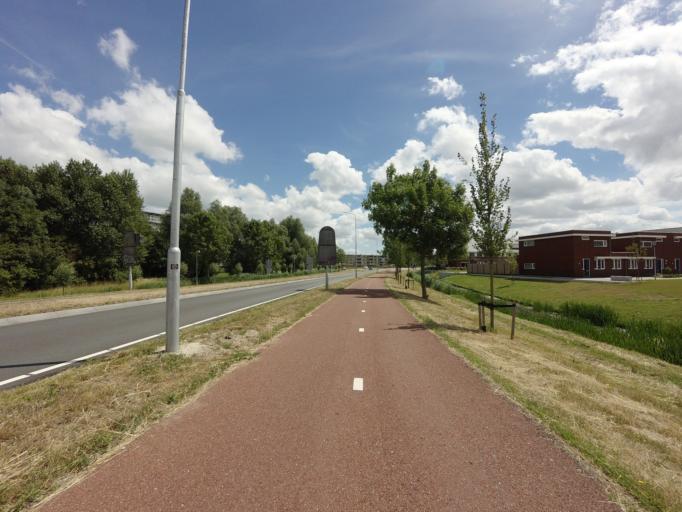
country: NL
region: North Holland
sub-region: Gemeente Zaanstad
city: Zaanstad
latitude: 52.4997
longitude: 4.7990
